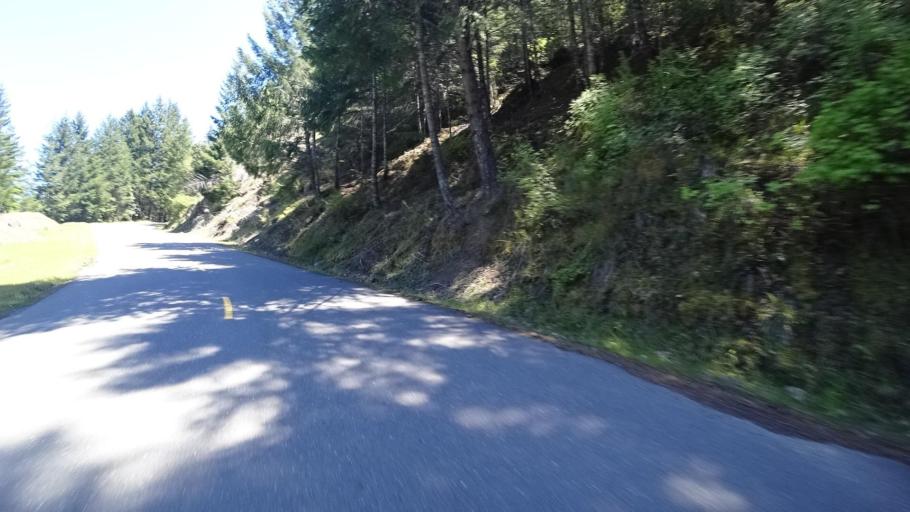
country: US
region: California
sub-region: Humboldt County
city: Rio Dell
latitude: 40.3255
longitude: -124.0533
